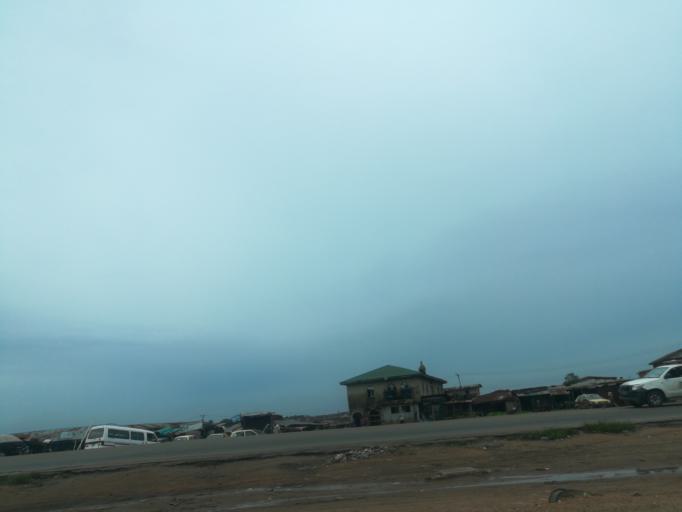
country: NG
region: Oyo
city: Ibadan
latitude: 7.3532
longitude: 3.9205
